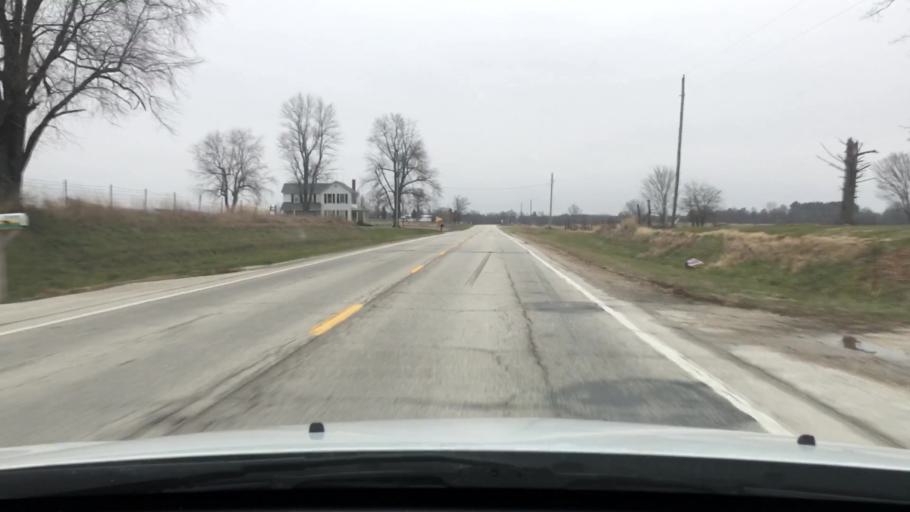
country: US
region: Illinois
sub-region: Pike County
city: Pittsfield
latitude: 39.5847
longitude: -90.9007
